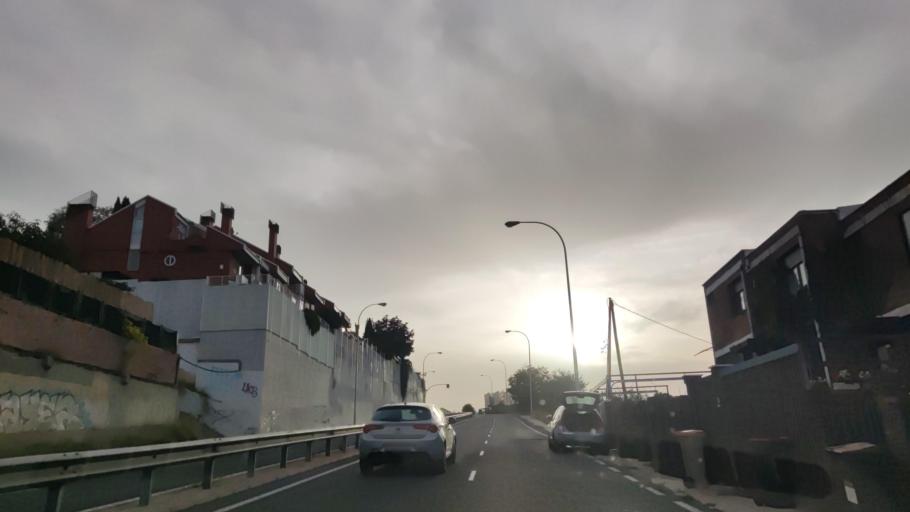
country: ES
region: Madrid
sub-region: Provincia de Madrid
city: Fuencarral-El Pardo
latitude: 40.4771
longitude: -3.7358
